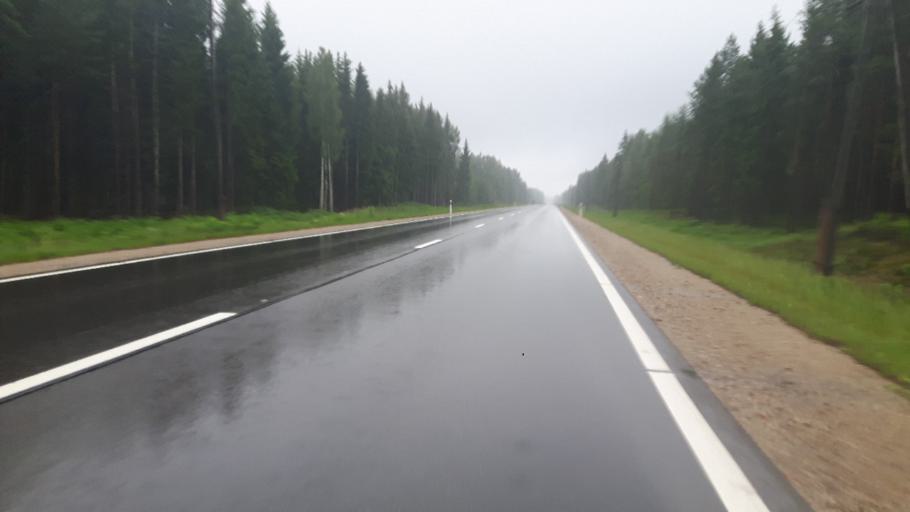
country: LV
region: Rucavas
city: Rucava
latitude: 56.1681
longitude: 21.1445
